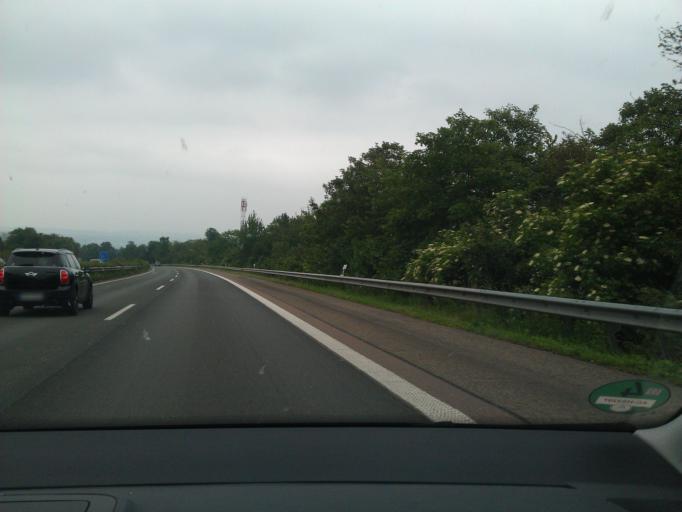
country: DE
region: Rheinland-Pfalz
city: Mulheim-Karlich
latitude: 50.3775
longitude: 7.5282
